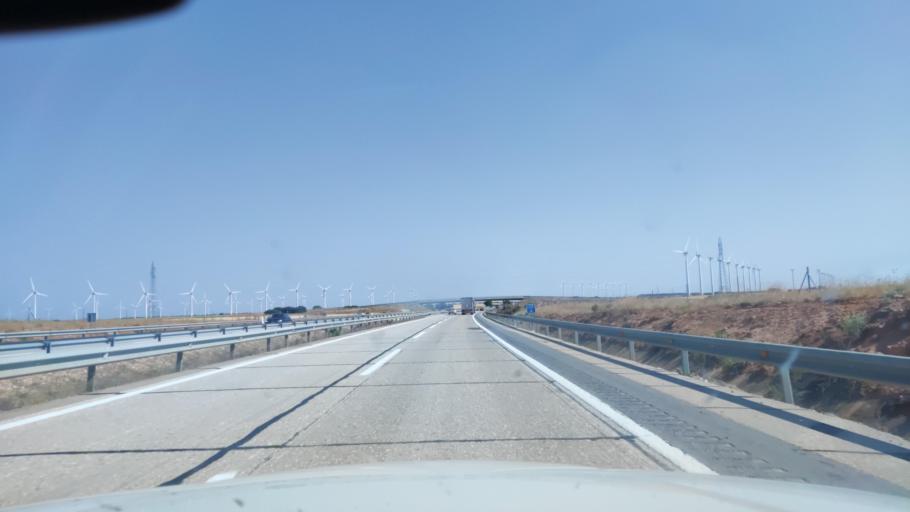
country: ES
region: Castille-La Mancha
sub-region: Provincia de Cuenca
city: Atalaya del Canavate
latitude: 39.4885
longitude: -2.2232
